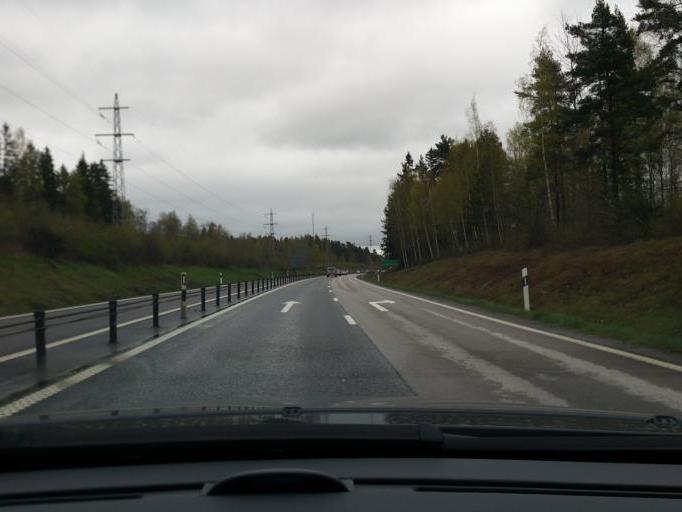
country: SE
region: Kronoberg
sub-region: Vaxjo Kommun
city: Vaexjoe
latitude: 56.8988
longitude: 14.7855
